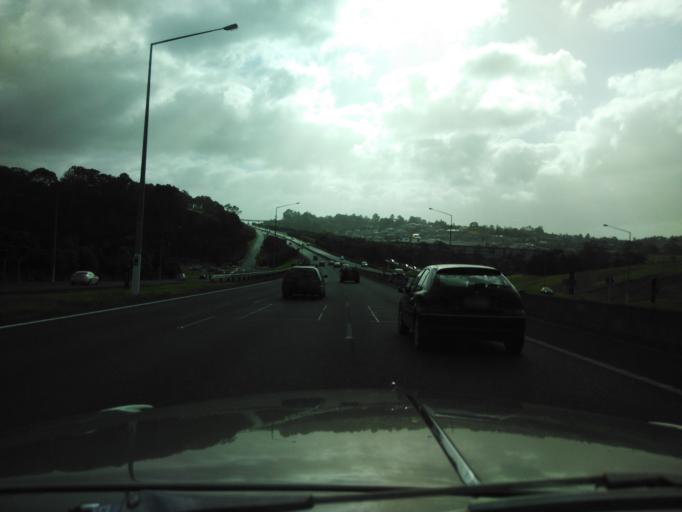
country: NZ
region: Auckland
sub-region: Auckland
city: Rothesay Bay
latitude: -36.7211
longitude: 174.7137
